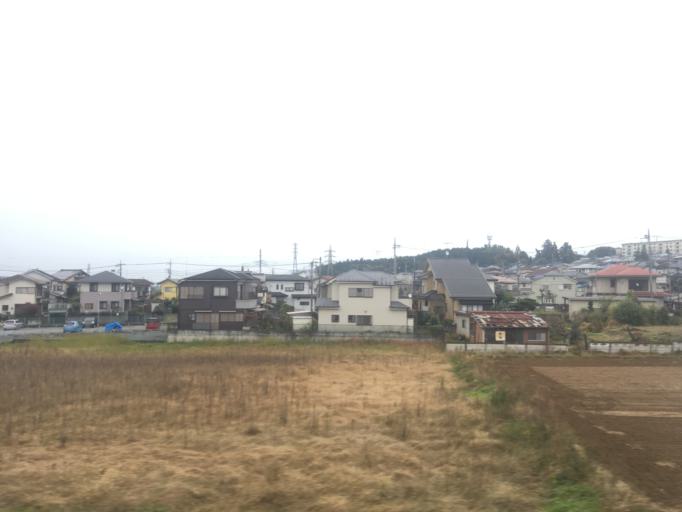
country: JP
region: Saitama
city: Hanno
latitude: 35.8897
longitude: 139.3417
